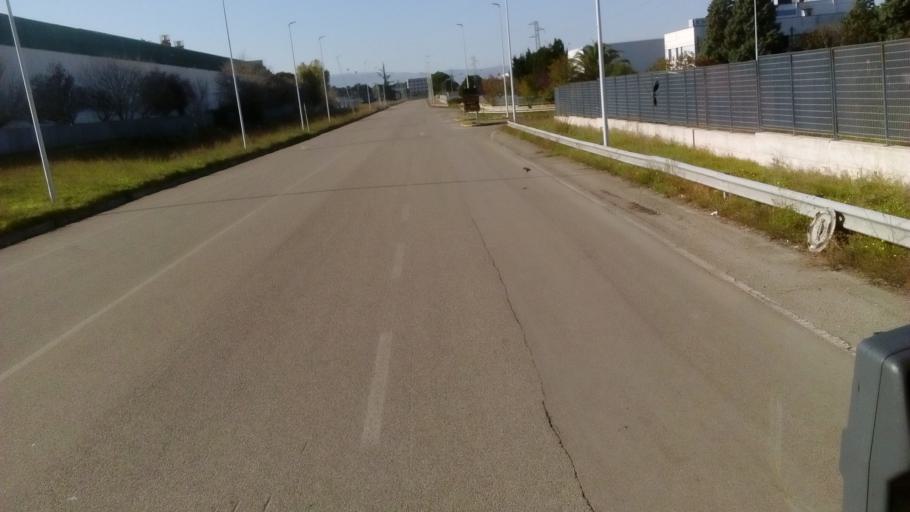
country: IT
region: Basilicate
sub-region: Provincia di Potenza
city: Melfi
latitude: 41.0760
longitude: 15.6838
